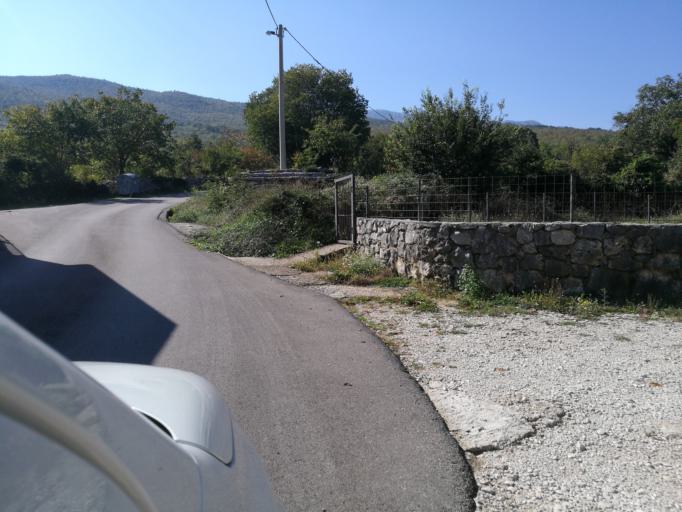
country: HR
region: Splitsko-Dalmatinska
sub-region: Grad Omis
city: Omis
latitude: 43.5154
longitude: 16.7354
